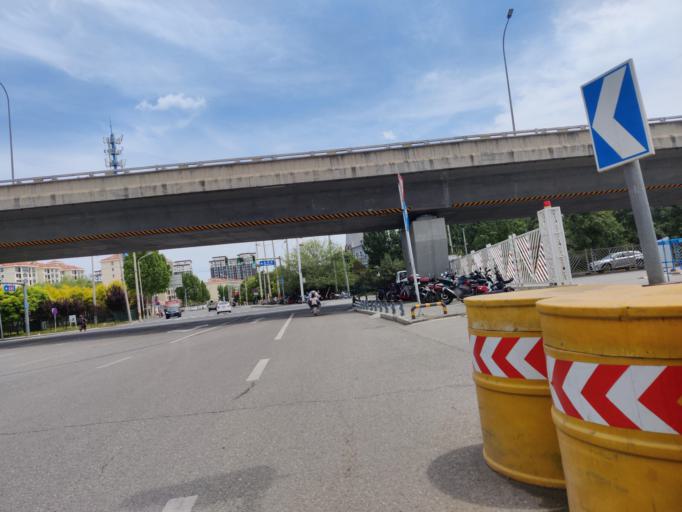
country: CN
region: Beijing
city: Miaocheng
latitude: 40.2878
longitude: 116.6363
